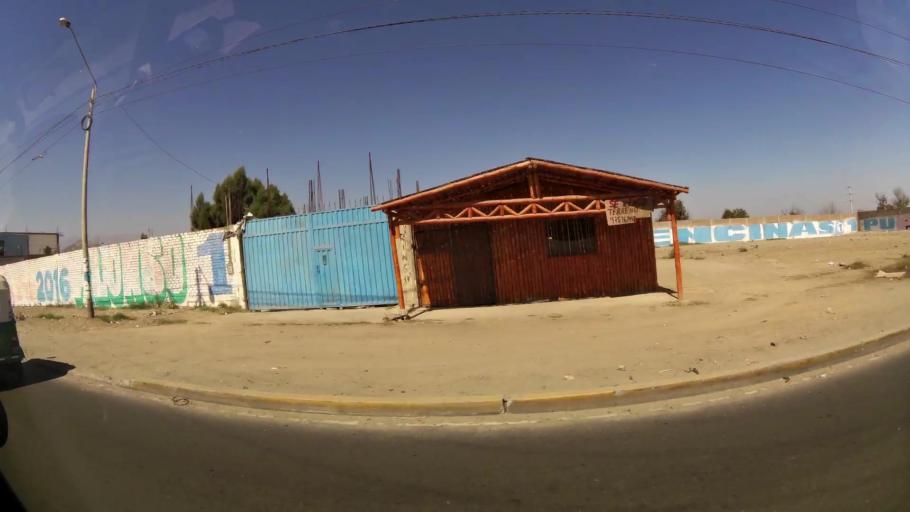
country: PE
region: Ica
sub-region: Provincia de Ica
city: La Tinguina
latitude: -14.0562
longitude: -75.7084
